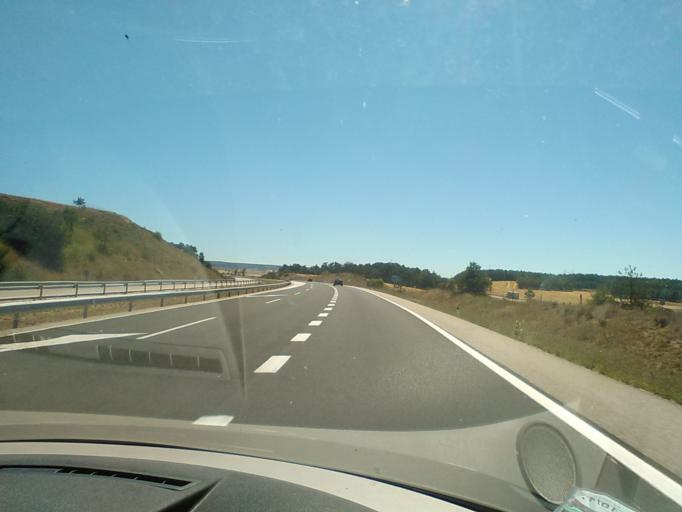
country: ES
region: Castille and Leon
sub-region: Provincia de Burgos
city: Fresno de Rodilla
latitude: 42.4372
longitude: -3.4975
